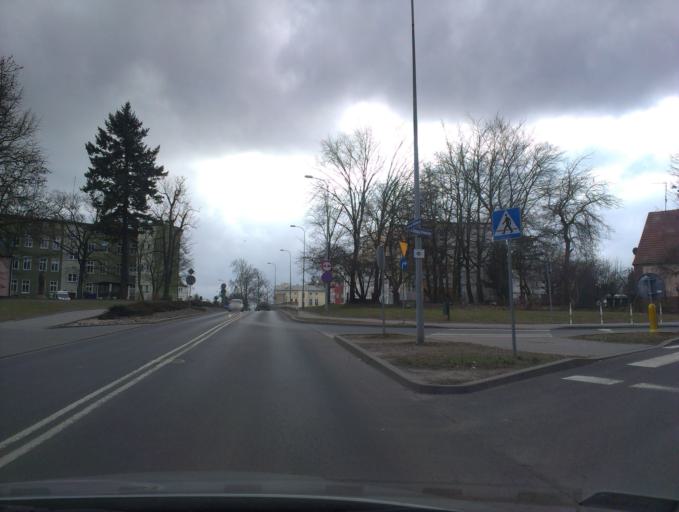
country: PL
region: West Pomeranian Voivodeship
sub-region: Koszalin
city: Koszalin
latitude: 54.1922
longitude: 16.1939
